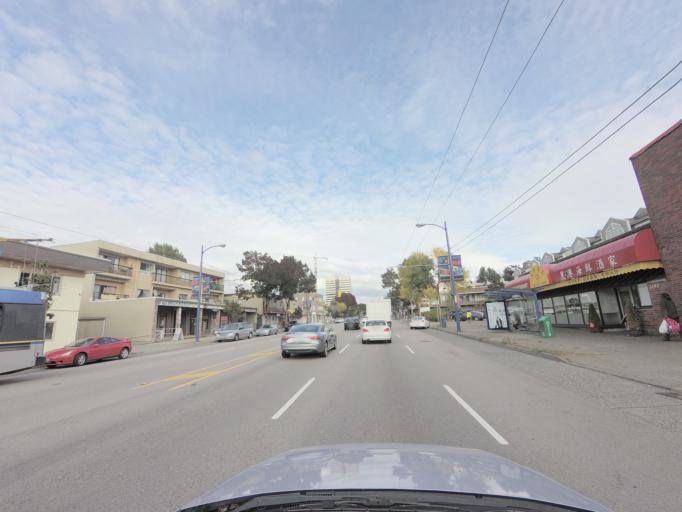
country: CA
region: British Columbia
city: Burnaby
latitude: 49.2320
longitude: -123.0292
